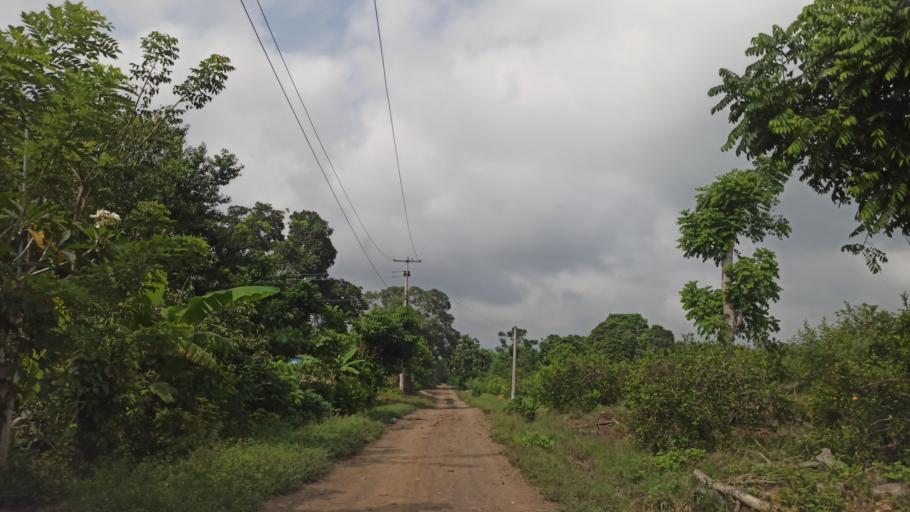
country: MX
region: Puebla
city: San Jose Acateno
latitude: 20.1611
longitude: -97.1824
